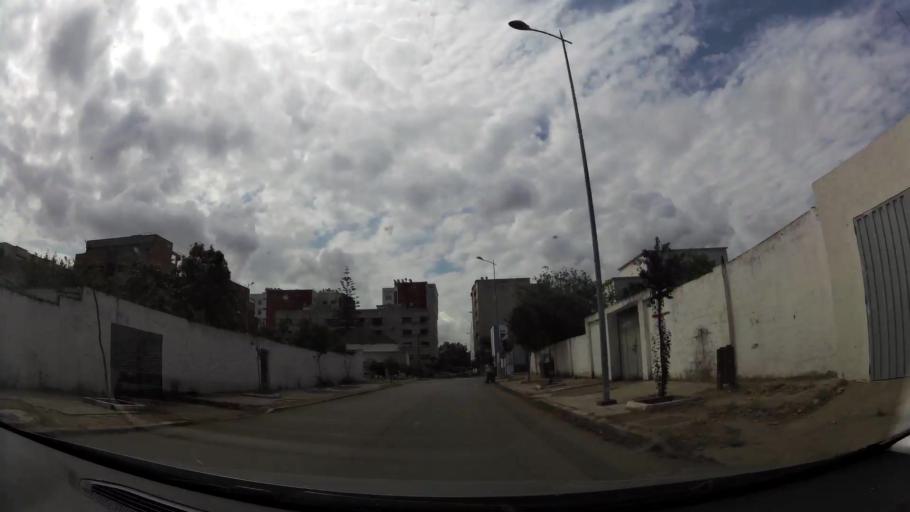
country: MA
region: Gharb-Chrarda-Beni Hssen
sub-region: Kenitra Province
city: Kenitra
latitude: 34.2562
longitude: -6.5777
